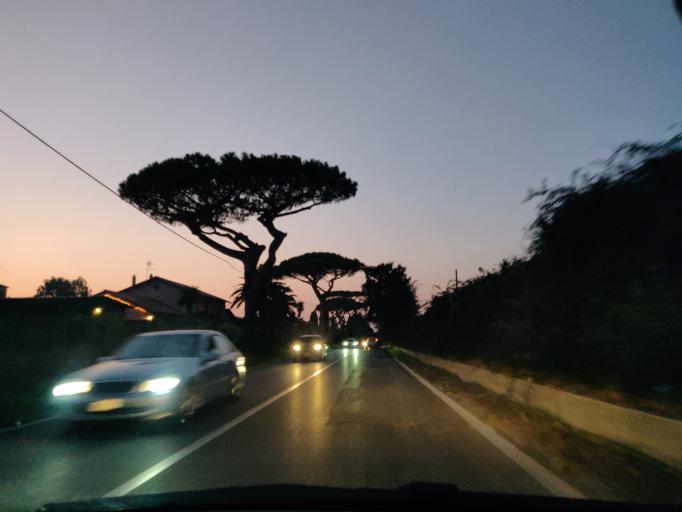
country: IT
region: Latium
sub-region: Citta metropolitana di Roma Capitale
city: Npp 23 (Parco Leonardo)
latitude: 41.8441
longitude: 12.2721
